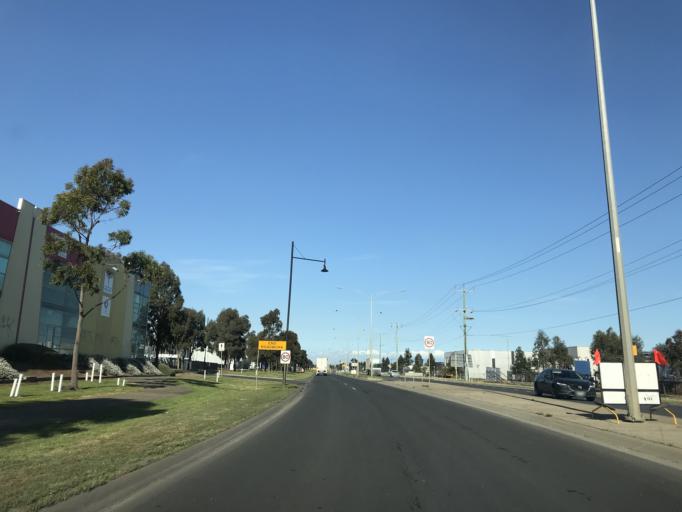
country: AU
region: Victoria
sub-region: Wyndham
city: Truganina
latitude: -37.8105
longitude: 144.7517
